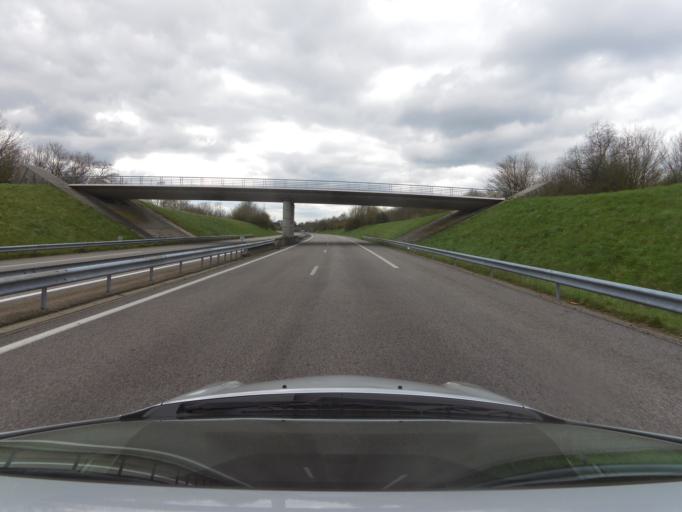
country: FR
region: Haute-Normandie
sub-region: Departement de la Seine-Maritime
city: Etainhus
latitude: 49.5681
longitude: 0.3468
